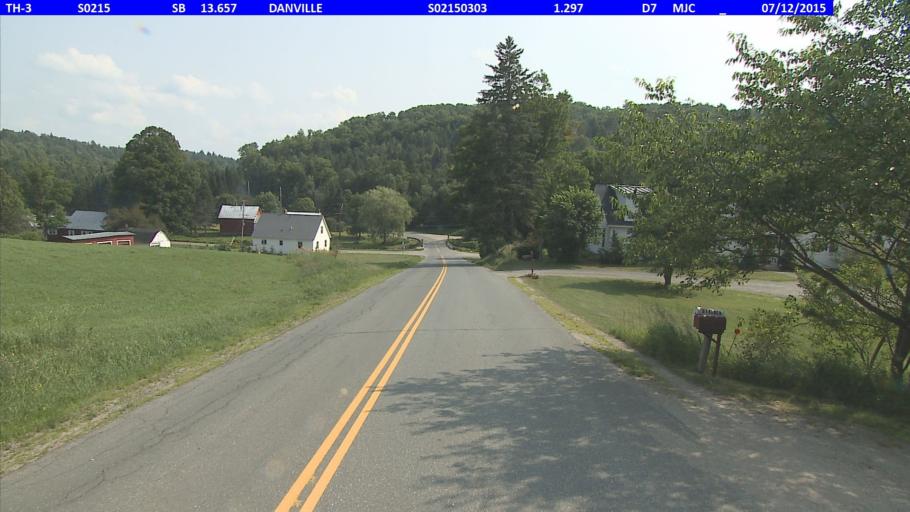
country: US
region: Vermont
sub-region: Caledonia County
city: Saint Johnsbury
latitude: 44.3844
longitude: -72.1444
